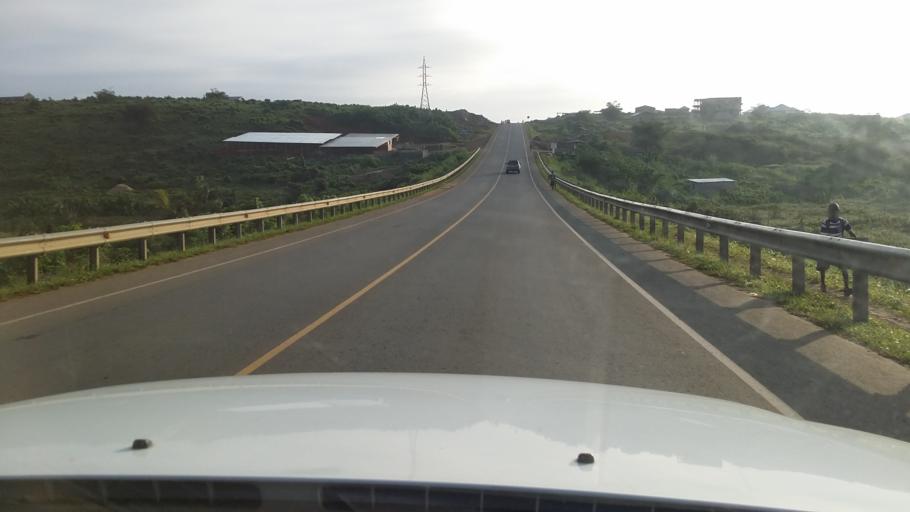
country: LR
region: Montserrado
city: Bensonville City
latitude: 6.3576
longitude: -10.6435
